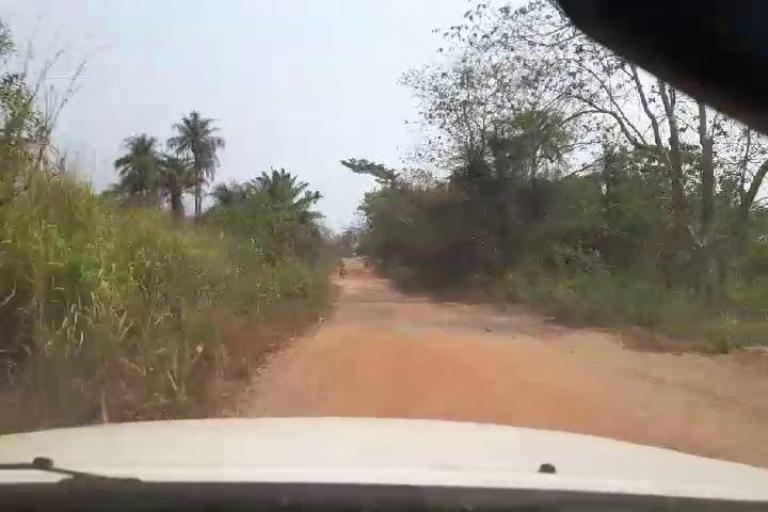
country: SL
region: Northern Province
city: Masingbi
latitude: 8.8696
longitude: -11.8183
